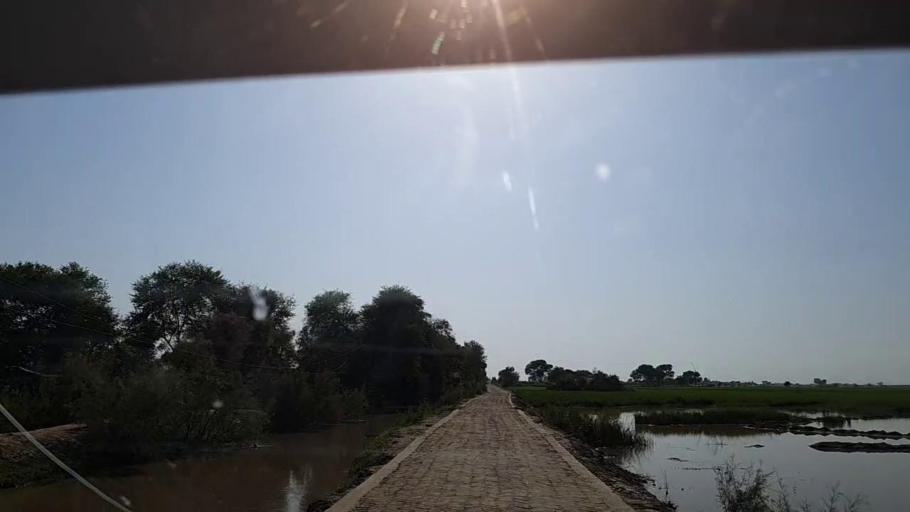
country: PK
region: Sindh
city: Tangwani
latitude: 28.2148
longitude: 68.9668
